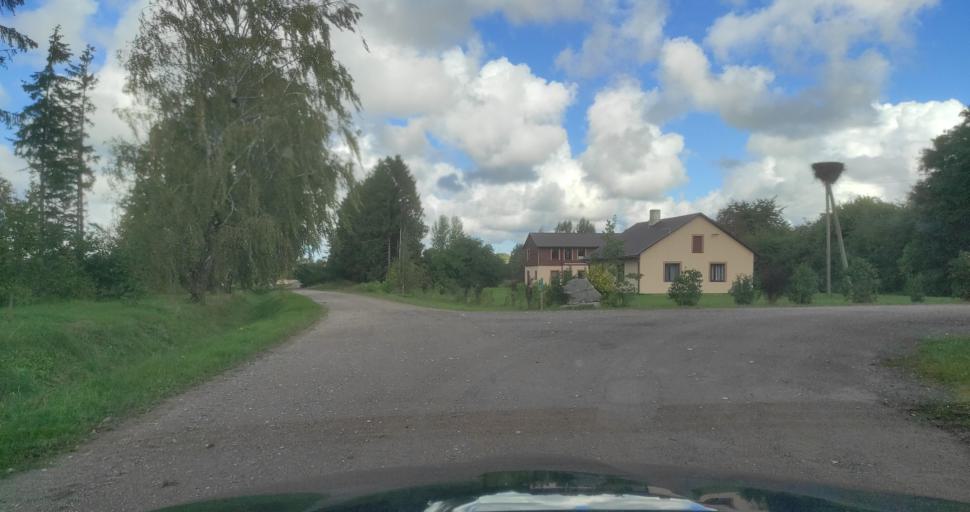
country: LV
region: Ventspils Rajons
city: Piltene
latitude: 57.2687
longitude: 21.5885
